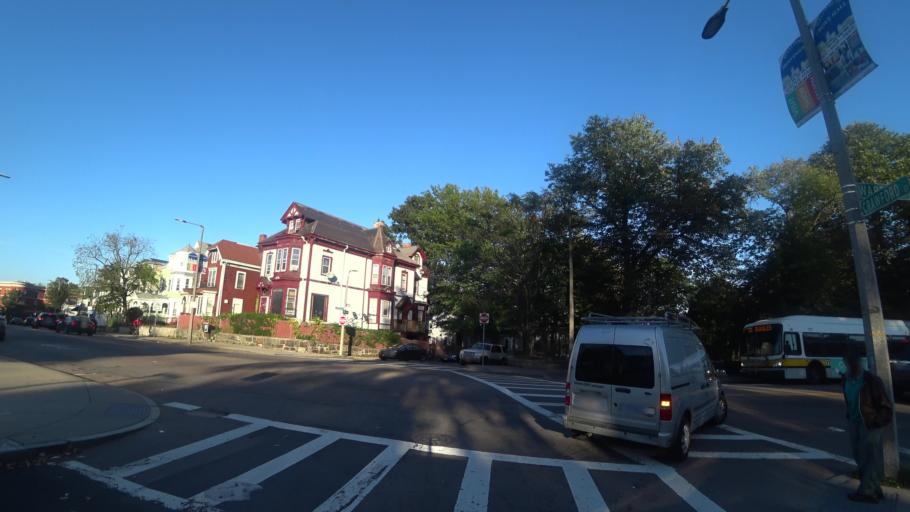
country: US
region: Massachusetts
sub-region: Suffolk County
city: Jamaica Plain
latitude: 42.3106
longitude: -71.0835
